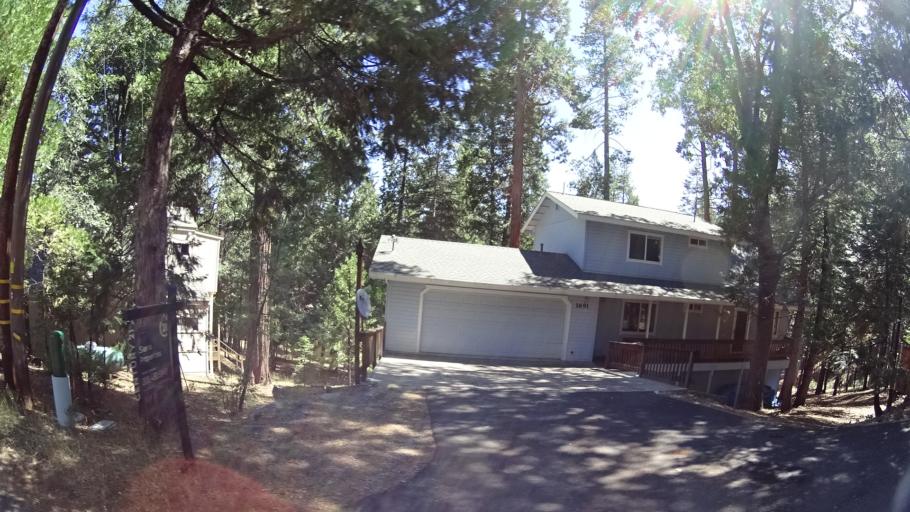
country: US
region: California
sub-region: Calaveras County
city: Arnold
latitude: 38.2417
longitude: -120.3371
